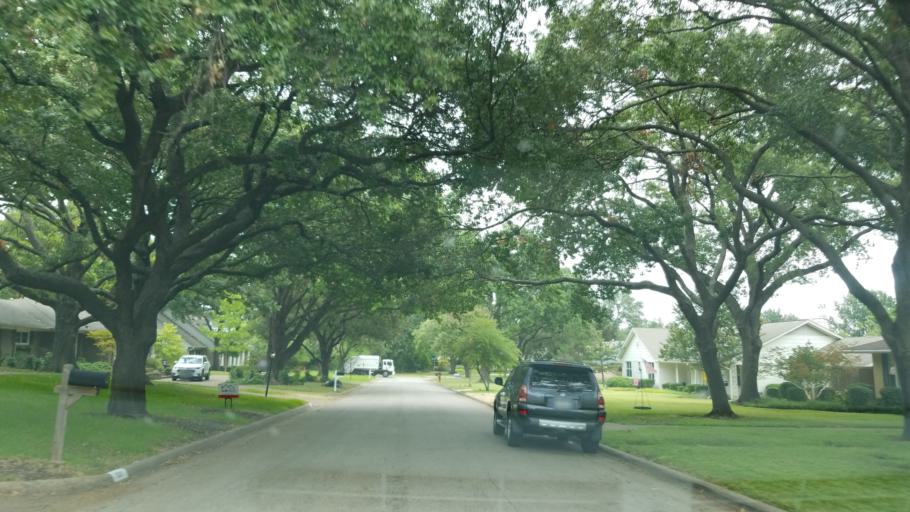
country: US
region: Texas
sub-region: Dallas County
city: Richardson
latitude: 32.9411
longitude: -96.7744
